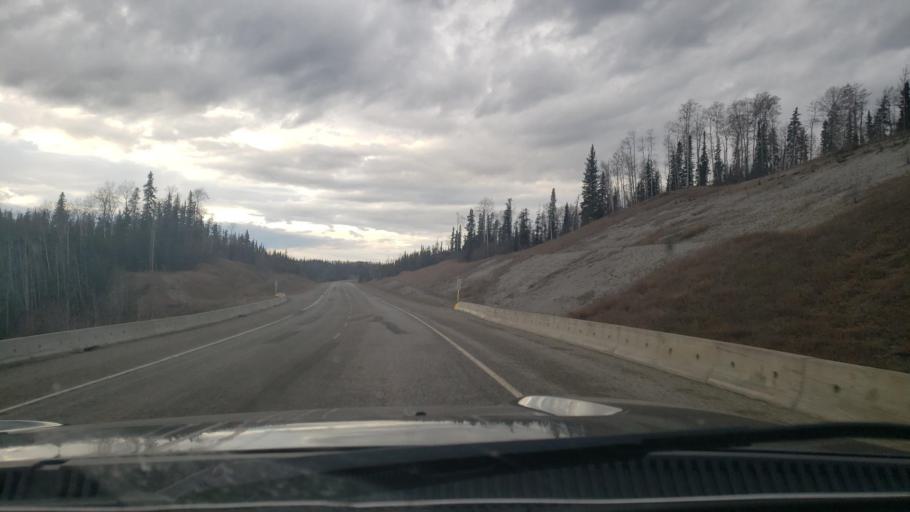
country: CA
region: Yukon
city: Watson Lake
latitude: 59.9795
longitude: -127.5732
